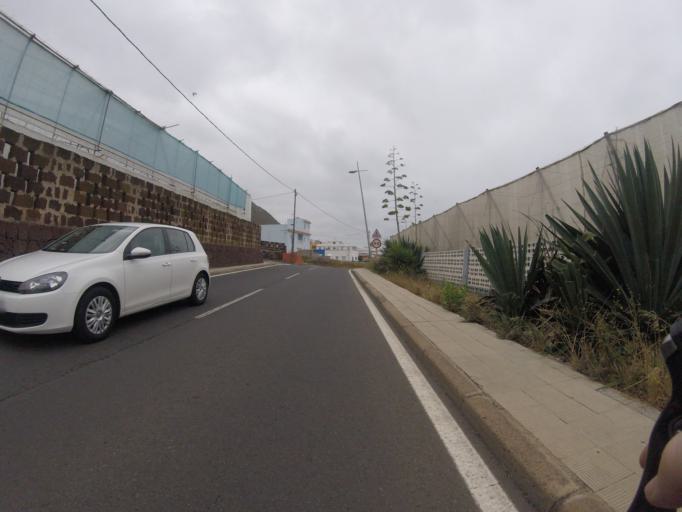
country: ES
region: Canary Islands
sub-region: Provincia de Santa Cruz de Tenerife
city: Tegueste
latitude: 28.5697
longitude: -16.3191
